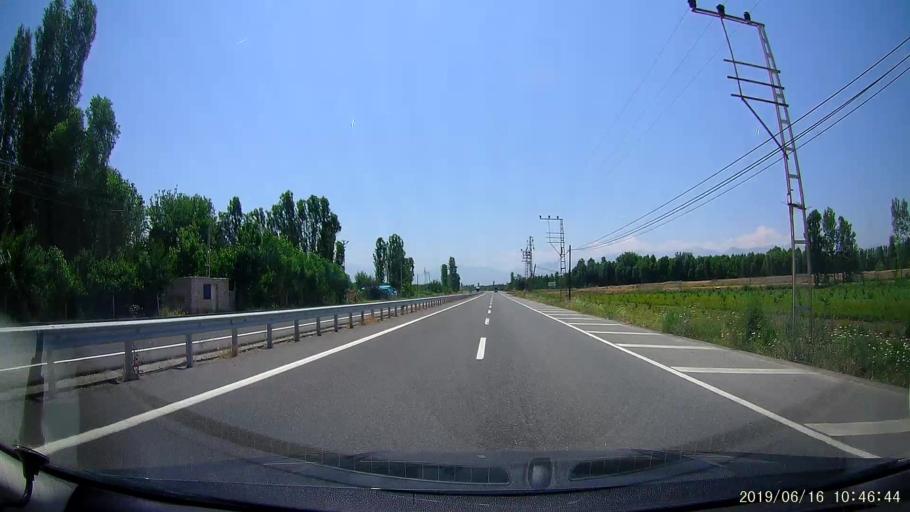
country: AM
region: Armavir
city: Shenavan
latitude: 40.0187
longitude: 43.8813
